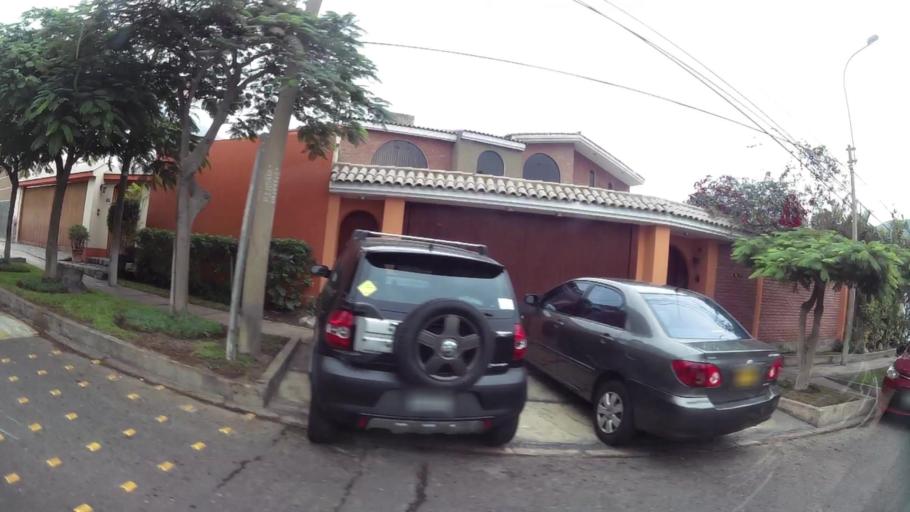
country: PE
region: Lima
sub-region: Lima
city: La Molina
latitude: -12.0925
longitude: -76.9237
